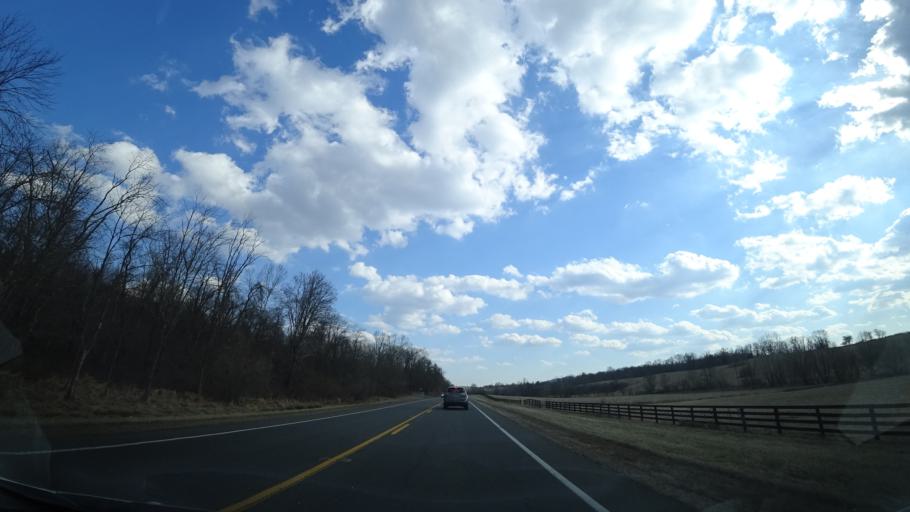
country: US
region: Virginia
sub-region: Fauquier County
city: Marshall
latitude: 38.9439
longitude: -77.9364
